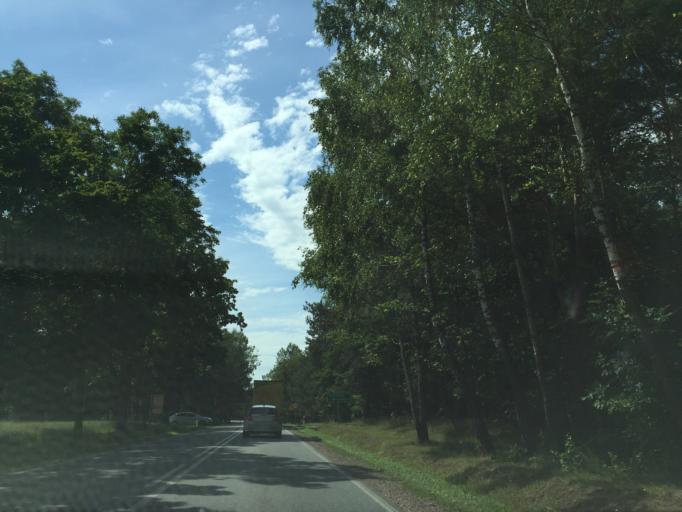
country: PL
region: Masovian Voivodeship
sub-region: Powiat losicki
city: Sarnaki
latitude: 52.3091
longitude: 22.8449
